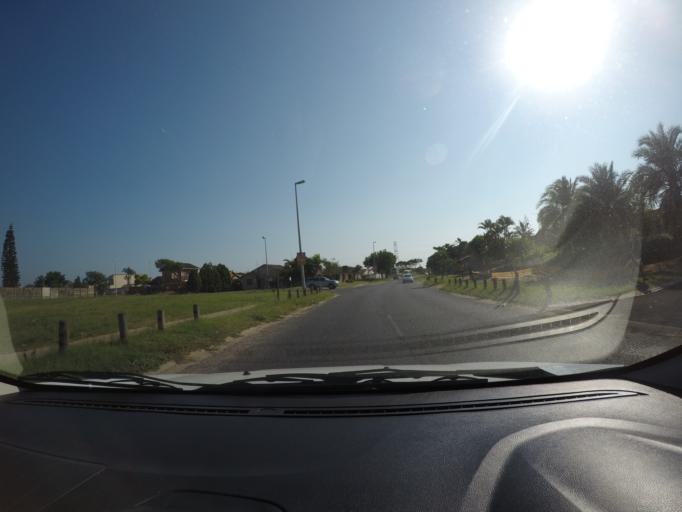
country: ZA
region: KwaZulu-Natal
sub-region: uThungulu District Municipality
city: Richards Bay
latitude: -28.7300
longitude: 32.0412
